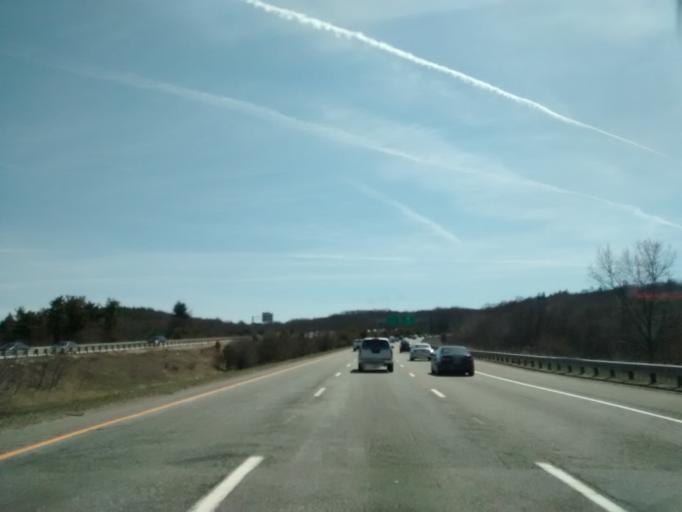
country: US
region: Massachusetts
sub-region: Middlesex County
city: Marlborough
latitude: 42.3070
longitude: -71.5659
